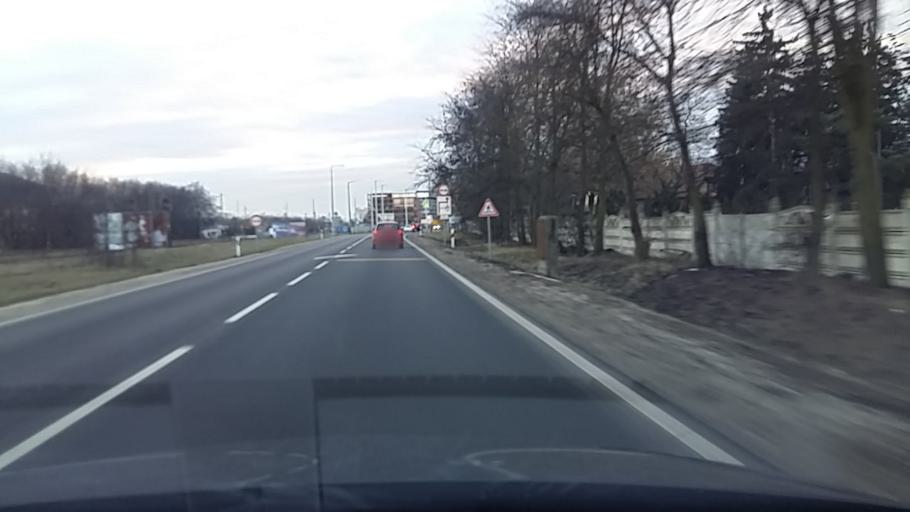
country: HU
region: Hajdu-Bihar
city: Debrecen
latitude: 47.5549
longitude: 21.6501
